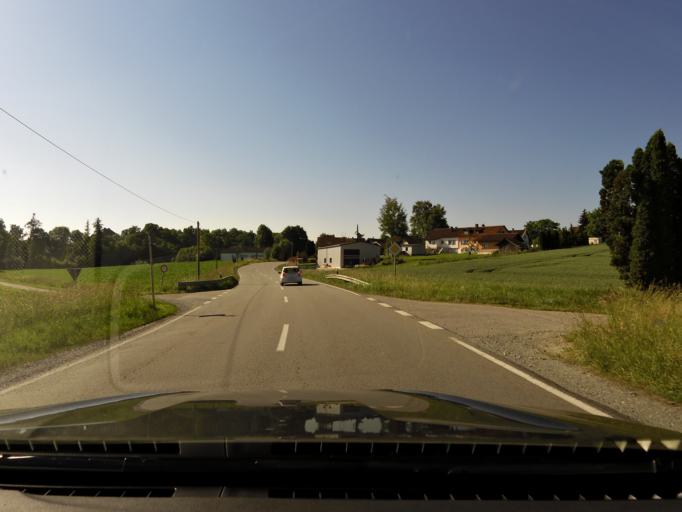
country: DE
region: Bavaria
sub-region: Upper Bavaria
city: Egglkofen
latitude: 48.4000
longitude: 12.4464
